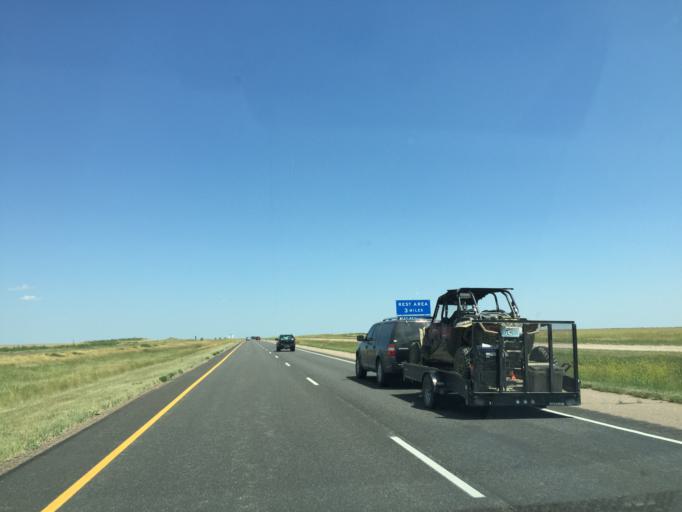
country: US
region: Colorado
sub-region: Lincoln County
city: Hugo
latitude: 39.2815
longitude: -103.3281
